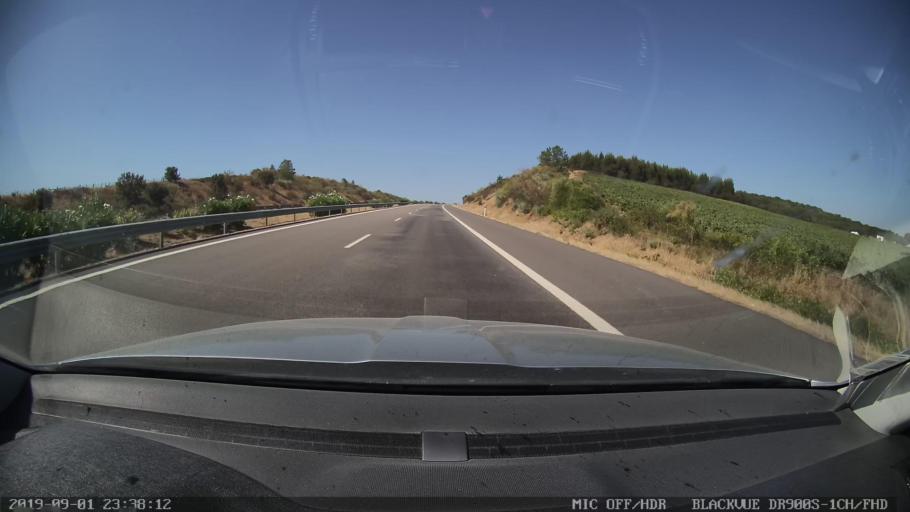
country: PT
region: Evora
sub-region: Borba
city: Borba
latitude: 38.8220
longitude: -7.4484
